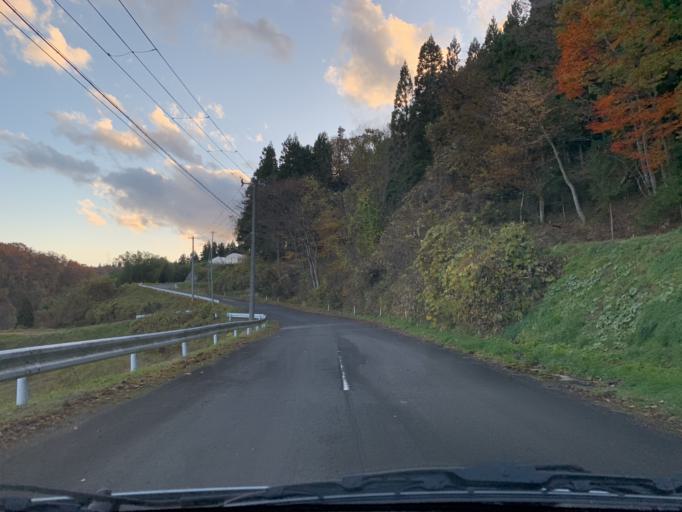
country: JP
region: Iwate
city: Mizusawa
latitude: 39.0280
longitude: 141.0366
